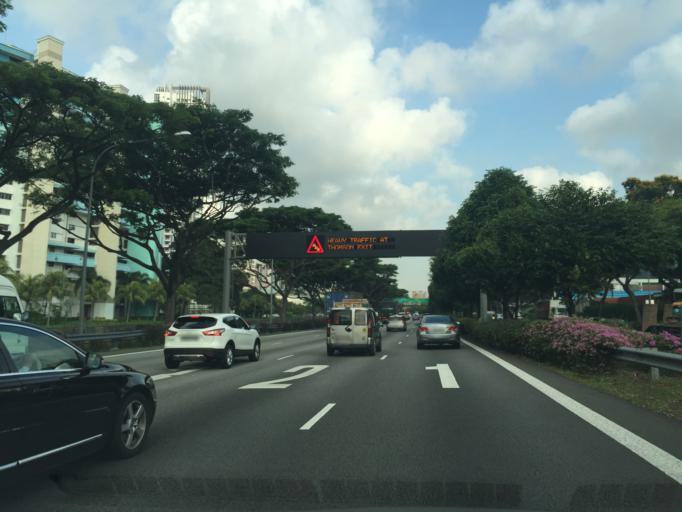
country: SG
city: Singapore
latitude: 1.3293
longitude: 103.8519
